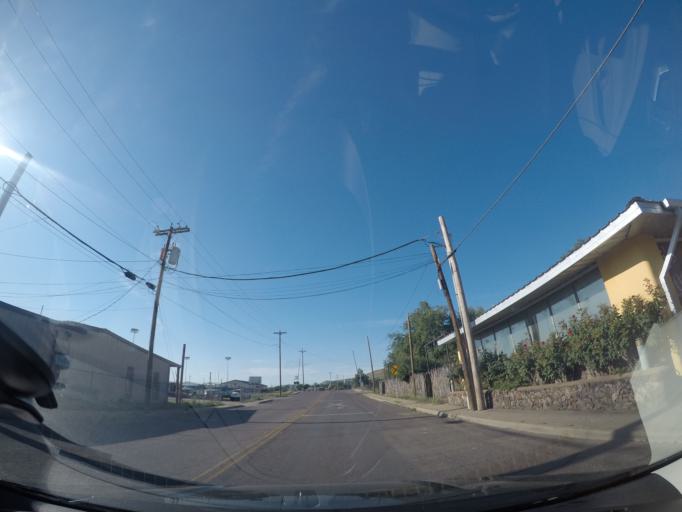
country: US
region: Texas
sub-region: Brewster County
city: Alpine
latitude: 30.3593
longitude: -103.6546
